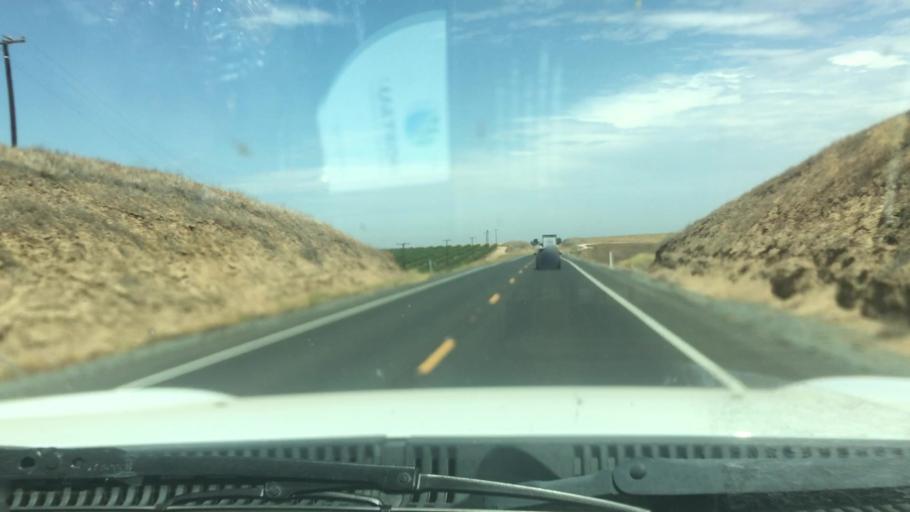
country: US
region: California
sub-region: Tulare County
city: Richgrove
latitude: 35.8000
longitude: -119.0535
